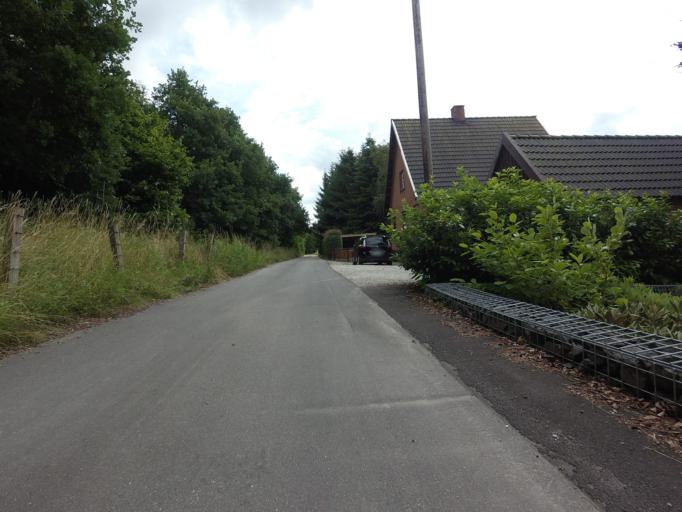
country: DK
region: Central Jutland
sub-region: Randers Kommune
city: Langa
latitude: 56.3562
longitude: 9.9120
